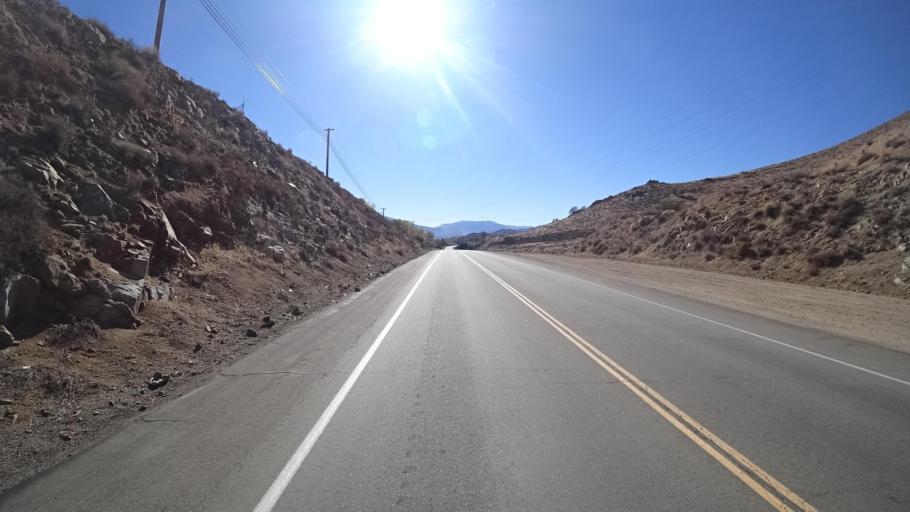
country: US
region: California
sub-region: Kern County
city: Kernville
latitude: 35.7292
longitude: -118.4298
